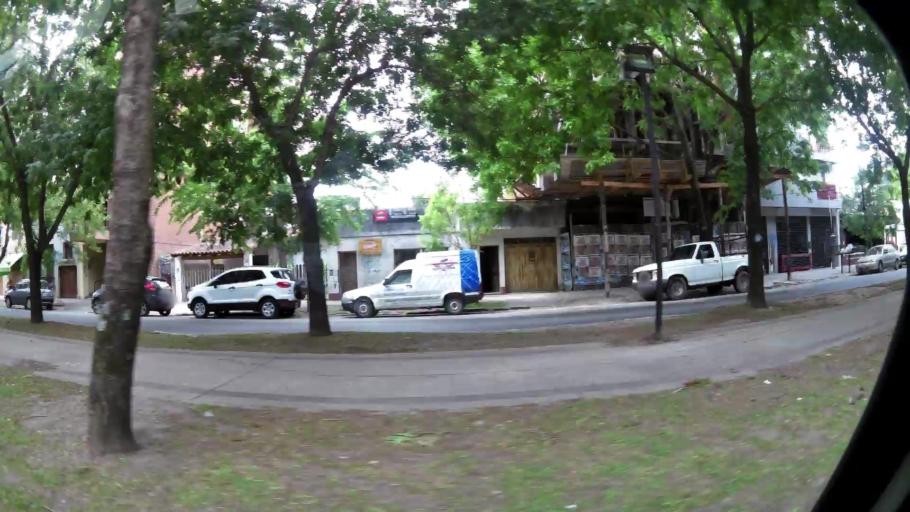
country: AR
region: Buenos Aires
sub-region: Partido de La Plata
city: La Plata
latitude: -34.9295
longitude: -57.9438
